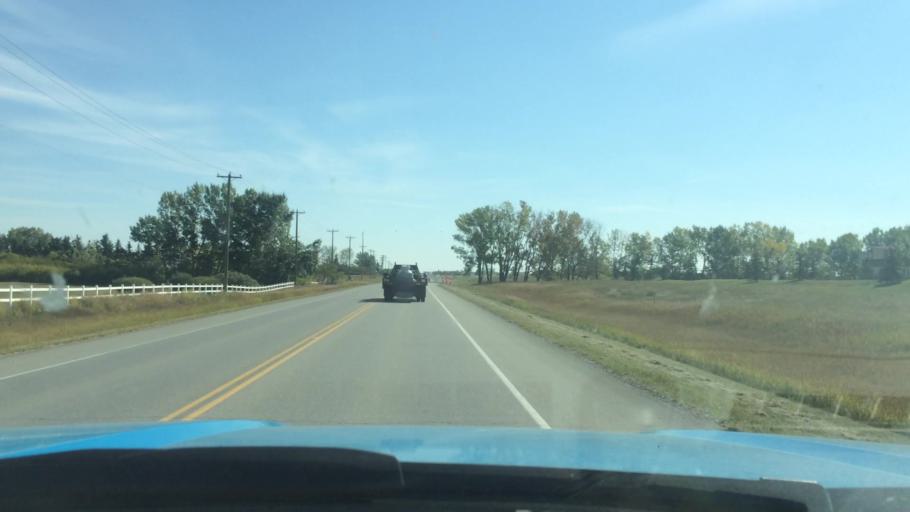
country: CA
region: Alberta
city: Airdrie
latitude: 51.2127
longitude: -113.9649
